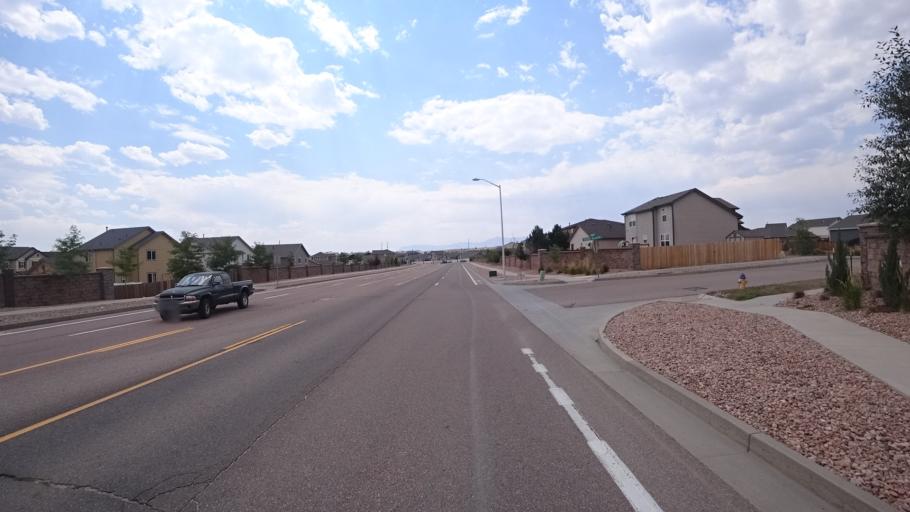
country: US
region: Colorado
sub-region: El Paso County
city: Black Forest
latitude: 38.9478
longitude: -104.6959
